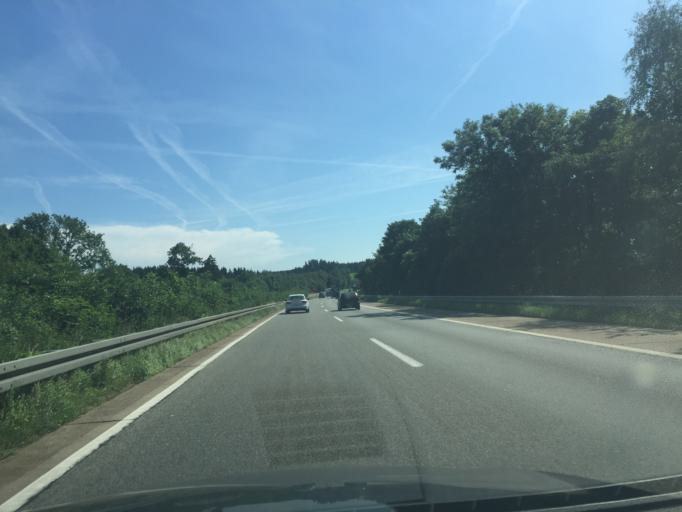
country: DE
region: North Rhine-Westphalia
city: Meinerzhagen
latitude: 51.1470
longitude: 7.6746
